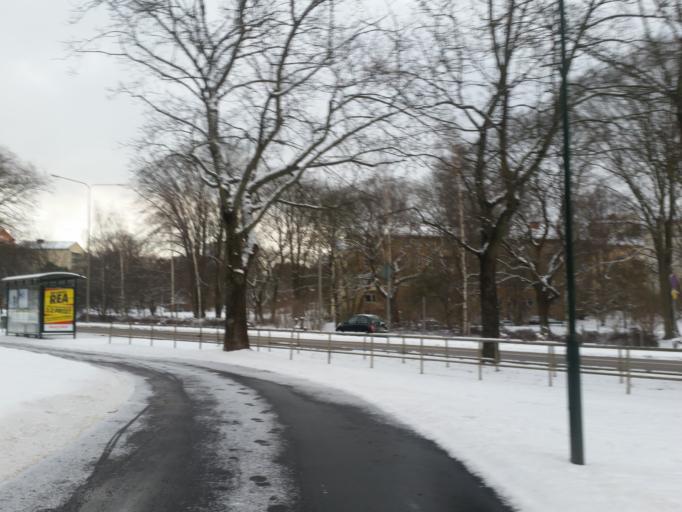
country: SE
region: Stockholm
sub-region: Stockholms Kommun
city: Arsta
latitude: 59.2966
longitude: 18.0698
